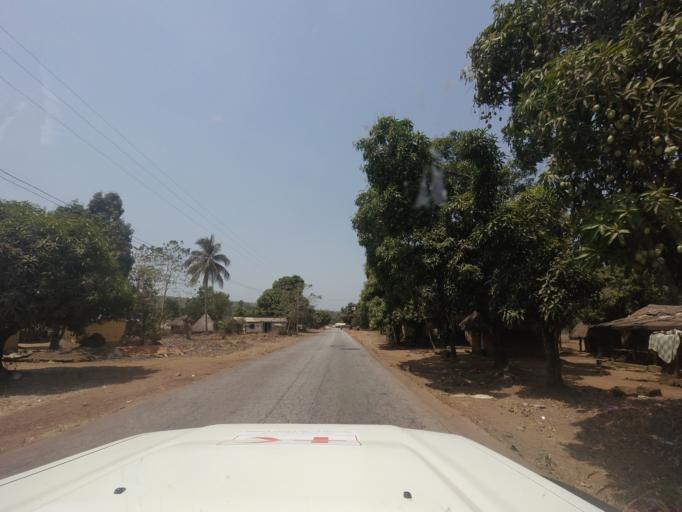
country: GN
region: Kindia
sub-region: Kindia
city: Kindia
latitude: 9.8615
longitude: -13.0798
